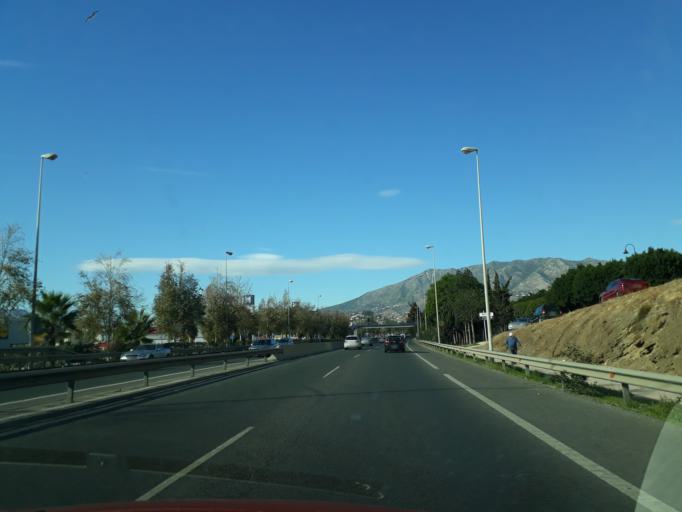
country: ES
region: Andalusia
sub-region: Provincia de Malaga
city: Fuengirola
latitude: 36.5343
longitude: -4.6326
